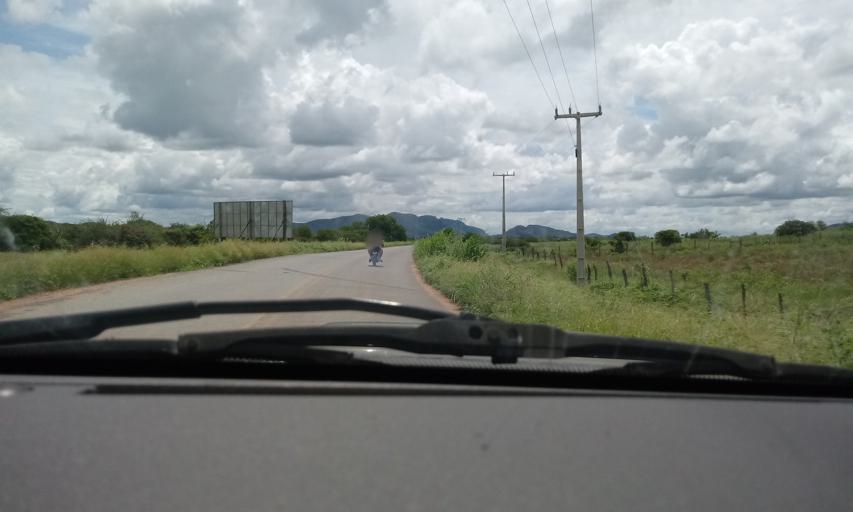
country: BR
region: Bahia
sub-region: Guanambi
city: Guanambi
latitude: -14.1936
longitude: -42.7969
